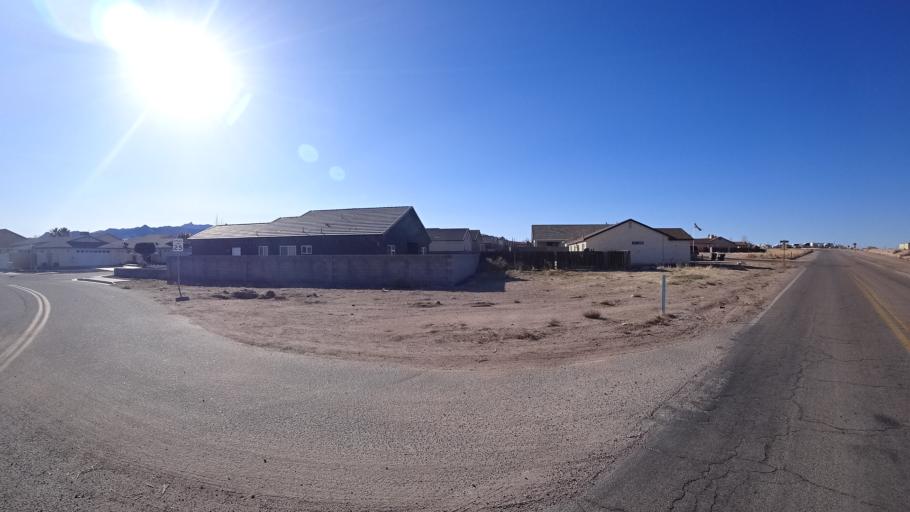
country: US
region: Arizona
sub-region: Mohave County
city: Kingman
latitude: 35.2140
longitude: -114.0098
